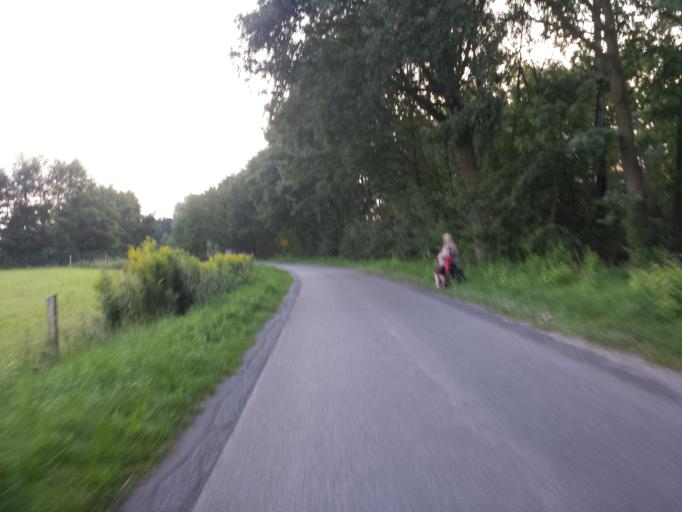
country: DE
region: North Rhine-Westphalia
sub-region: Regierungsbezirk Detmold
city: Harsewinkel
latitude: 51.9740
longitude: 8.2428
